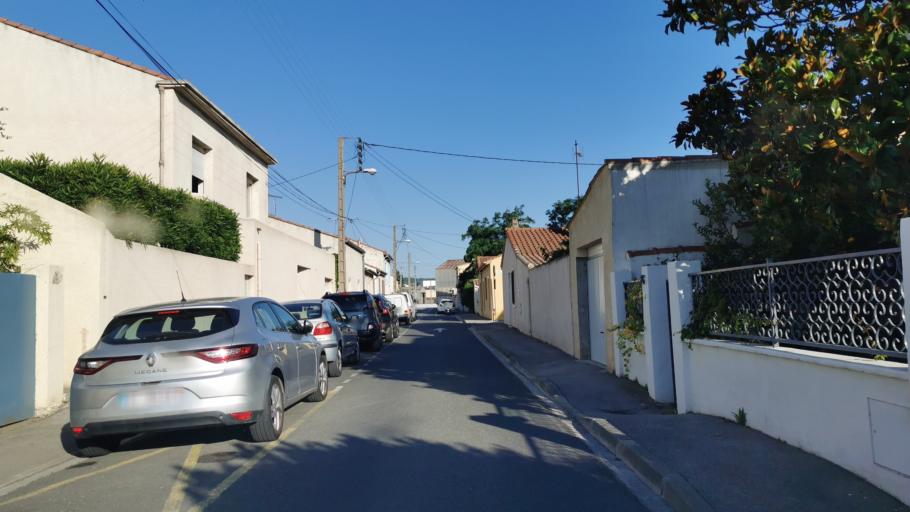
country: FR
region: Languedoc-Roussillon
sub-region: Departement de l'Aude
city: Narbonne
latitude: 43.1803
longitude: 2.9939
